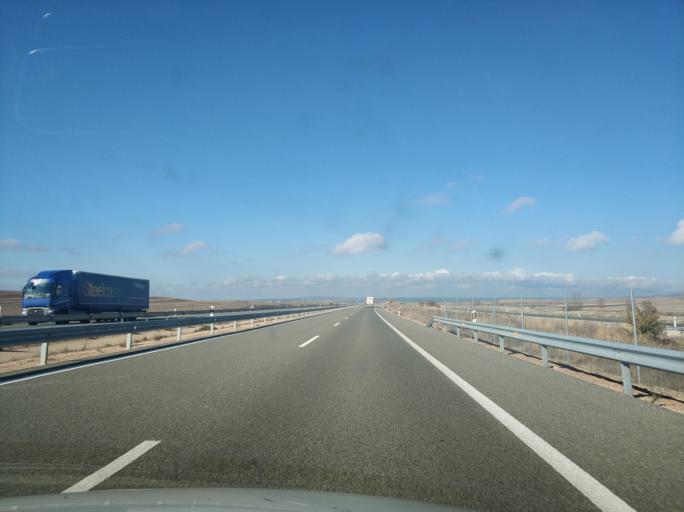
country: ES
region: Castille and Leon
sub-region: Provincia de Soria
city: Coscurita
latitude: 41.3997
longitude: -2.4768
